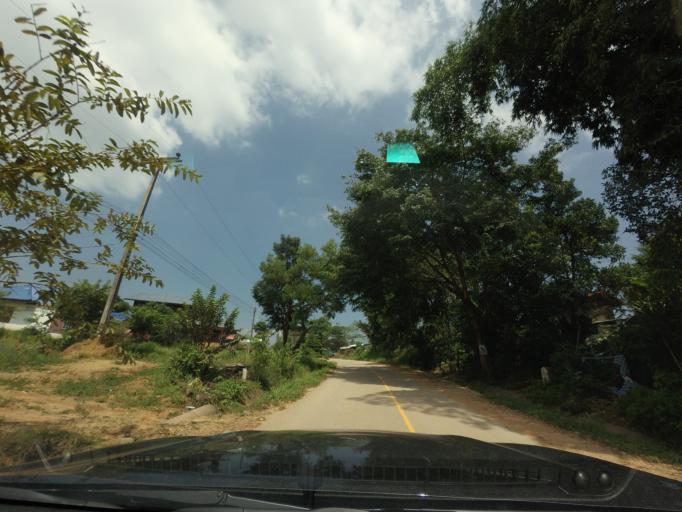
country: TH
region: Loei
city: Na Haeo
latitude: 17.5205
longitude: 100.8805
